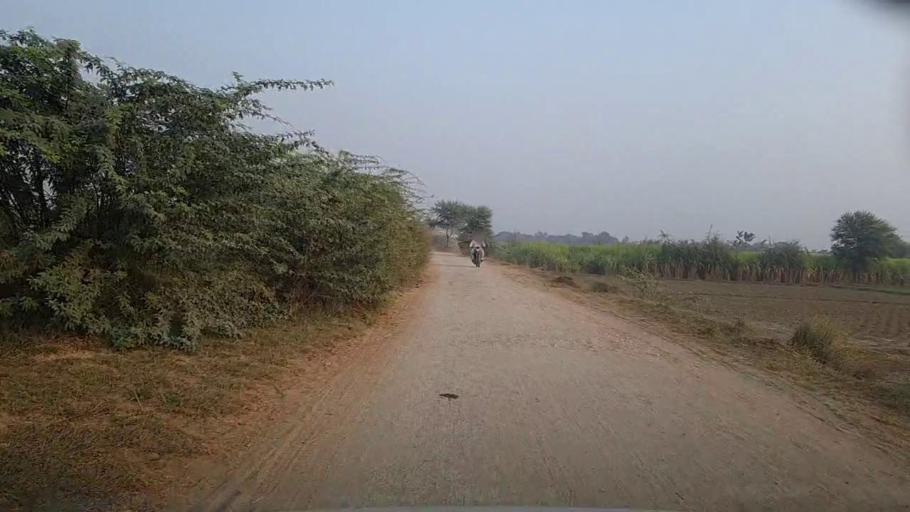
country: PK
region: Sindh
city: Bozdar
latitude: 27.0745
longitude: 68.5889
